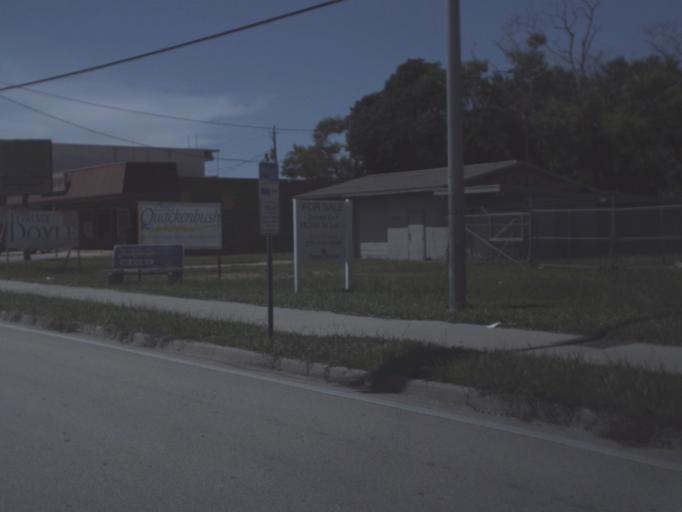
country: US
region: Florida
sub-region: Lee County
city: Fort Myers Beach
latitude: 26.4635
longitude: -81.9521
